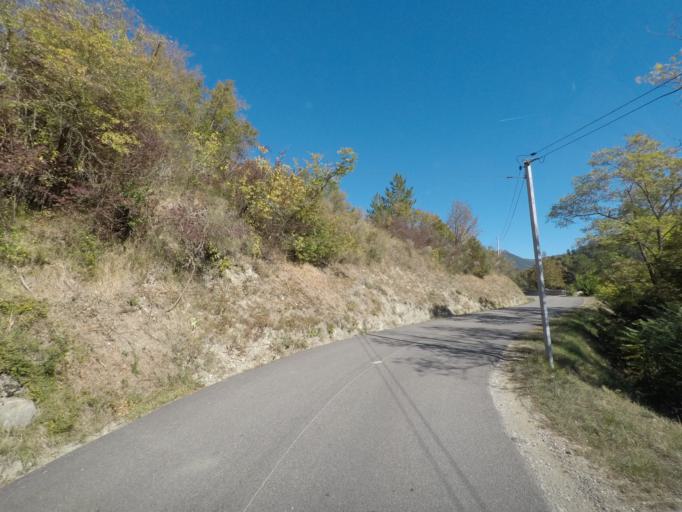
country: FR
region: Rhone-Alpes
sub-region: Departement de la Drome
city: Die
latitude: 44.6089
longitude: 5.2925
